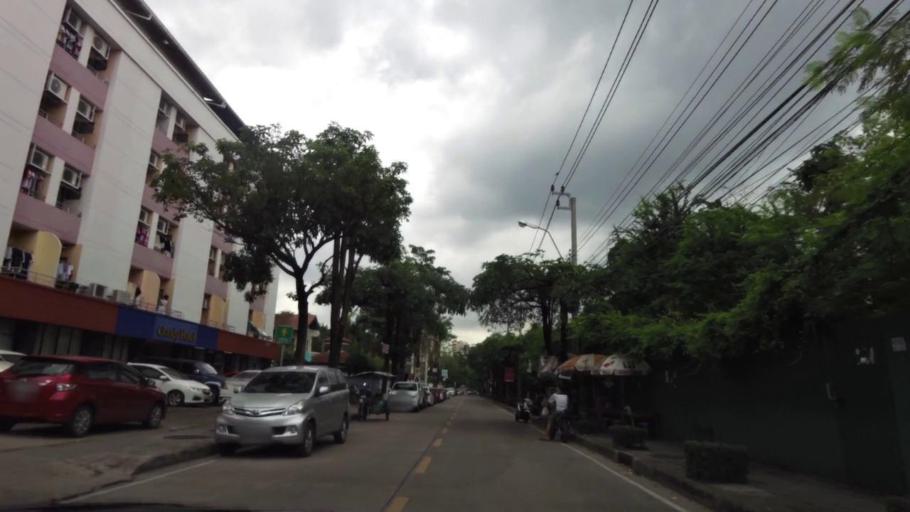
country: TH
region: Bangkok
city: Bang Kapi
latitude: 13.7571
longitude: 100.6394
